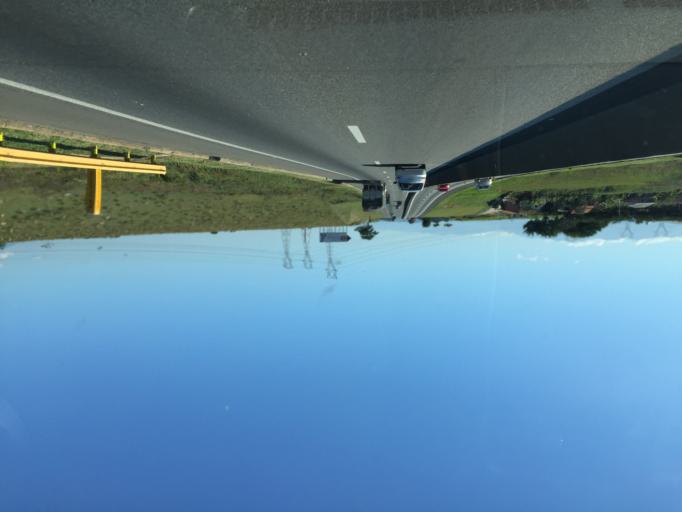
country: BR
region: Sao Paulo
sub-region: Lorena
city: Lorena
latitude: -22.7395
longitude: -45.0892
